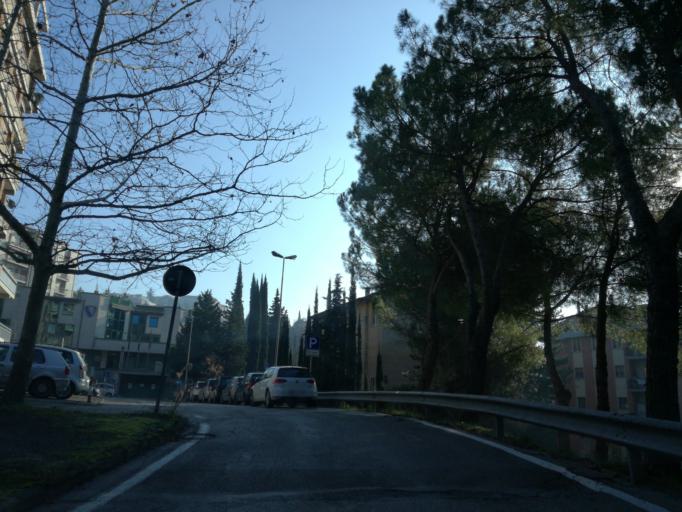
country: IT
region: Umbria
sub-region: Provincia di Perugia
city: Perugia
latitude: 43.1105
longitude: 12.3771
